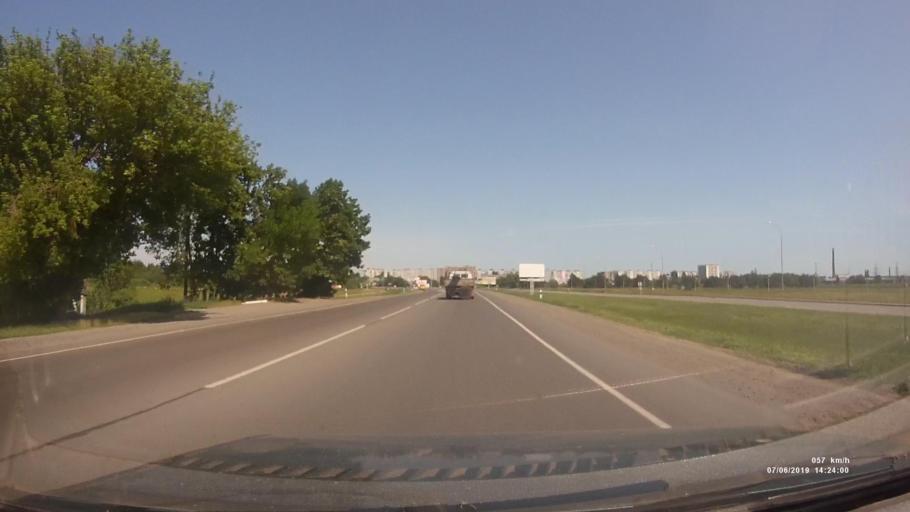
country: RU
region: Rostov
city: Kuleshovka
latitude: 47.0817
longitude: 39.5238
